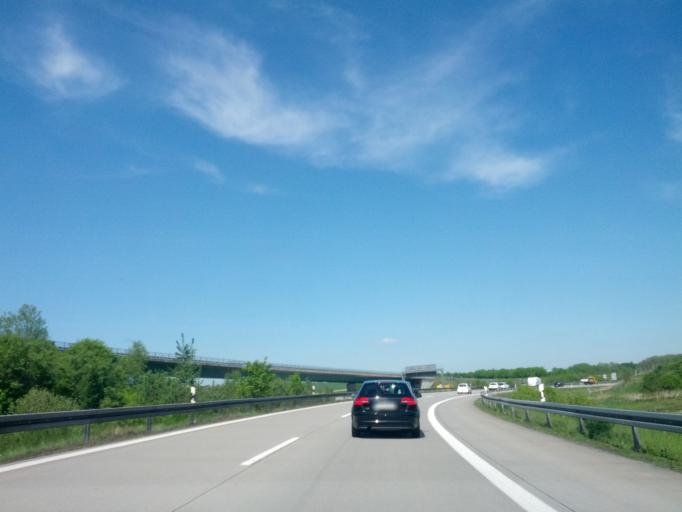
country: DE
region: Saxony
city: Wittgensdorf
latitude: 50.8508
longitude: 12.8460
